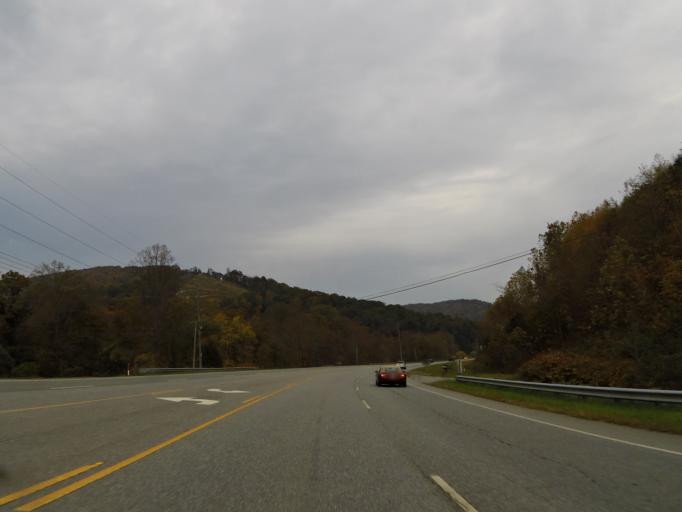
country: US
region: North Carolina
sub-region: Caldwell County
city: Lenoir
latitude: 36.0261
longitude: -81.5799
